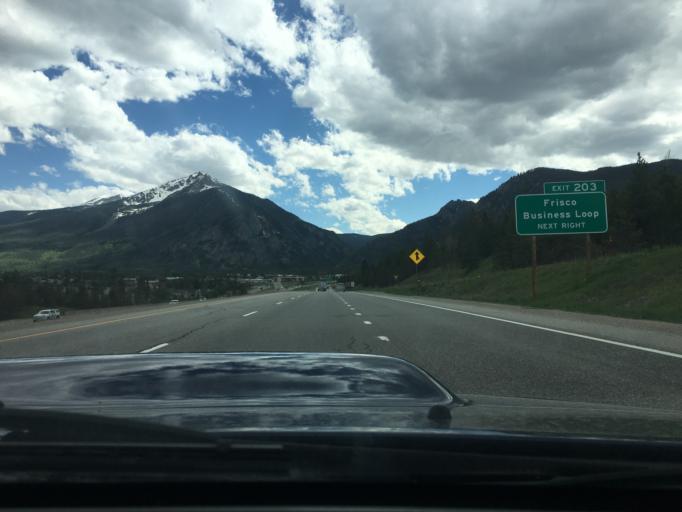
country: US
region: Colorado
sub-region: Summit County
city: Frisco
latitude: 39.5999
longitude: -106.0905
